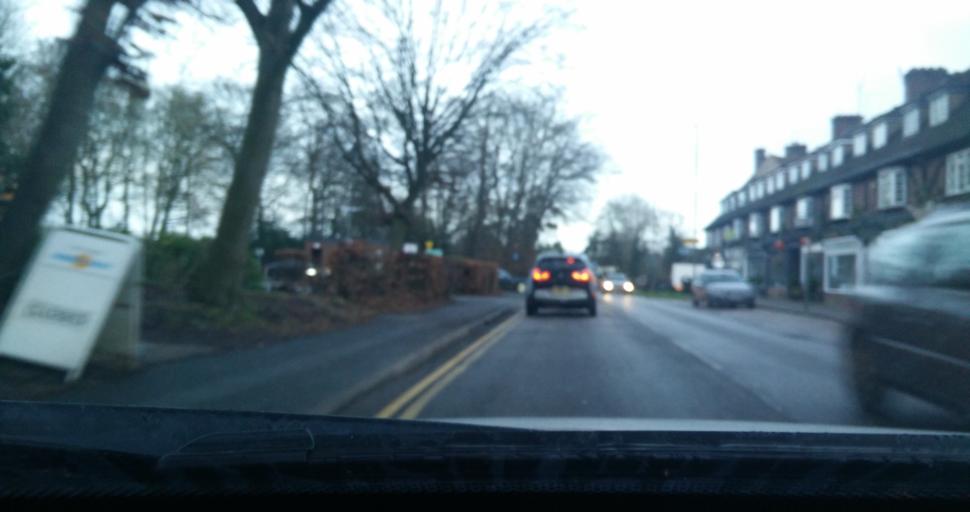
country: GB
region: England
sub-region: Buckinghamshire
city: Little Chalfont
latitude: 51.6663
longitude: -0.5664
